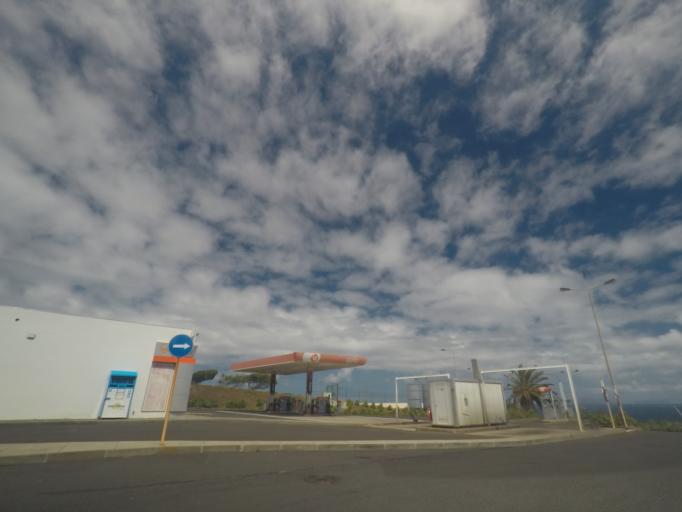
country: PT
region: Madeira
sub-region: Machico
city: Canical
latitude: 32.7429
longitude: -16.7363
